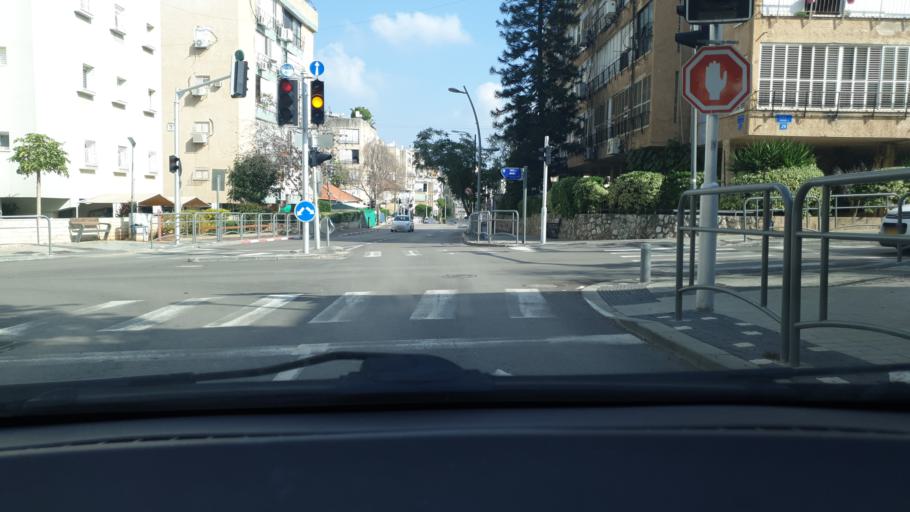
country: IL
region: Central District
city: Rishon LeZiyyon
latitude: 31.9667
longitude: 34.8062
